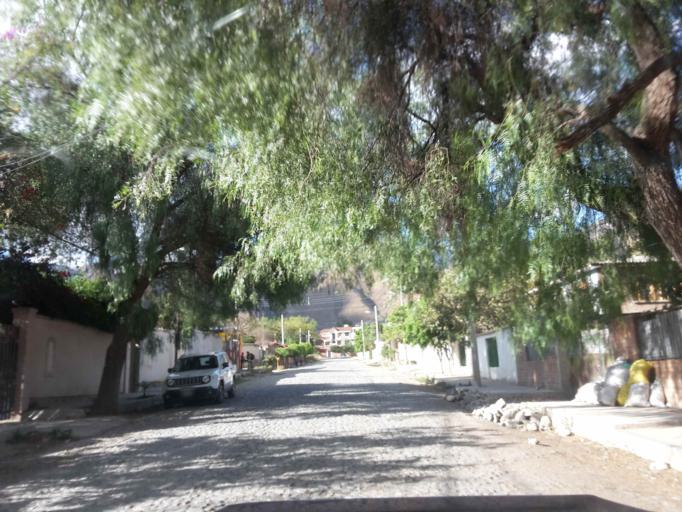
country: BO
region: Cochabamba
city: Cochabamba
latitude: -17.3519
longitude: -66.1996
